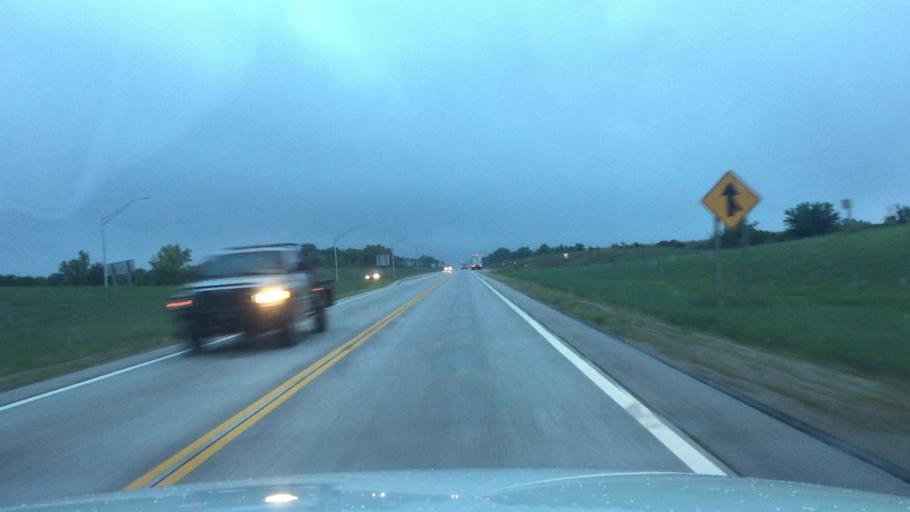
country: US
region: Kansas
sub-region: Neosho County
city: Chanute
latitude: 37.6449
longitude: -95.4797
